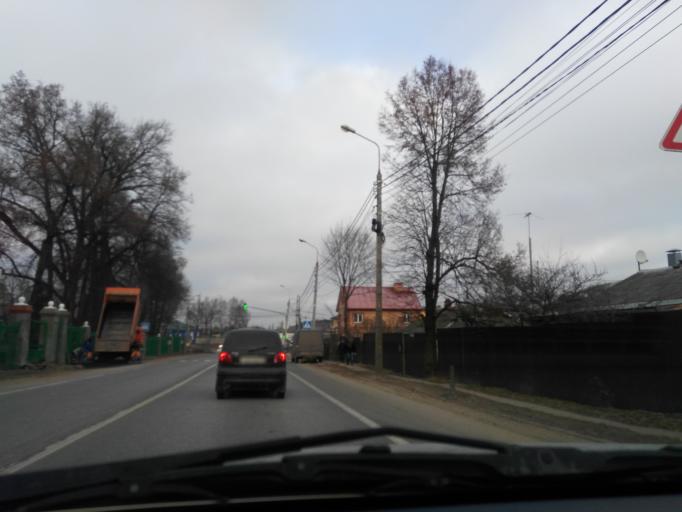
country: RU
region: Moskovskaya
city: Troitsk
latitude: 55.3174
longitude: 37.1537
